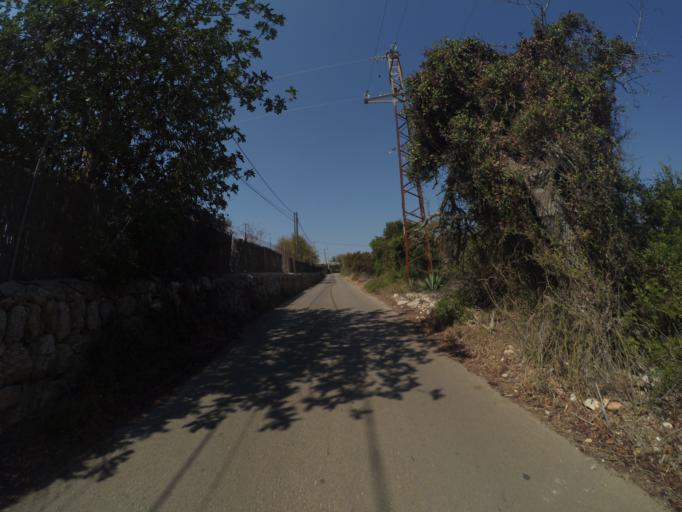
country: ES
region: Balearic Islands
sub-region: Illes Balears
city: Santanyi
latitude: 39.3905
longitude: 3.2382
